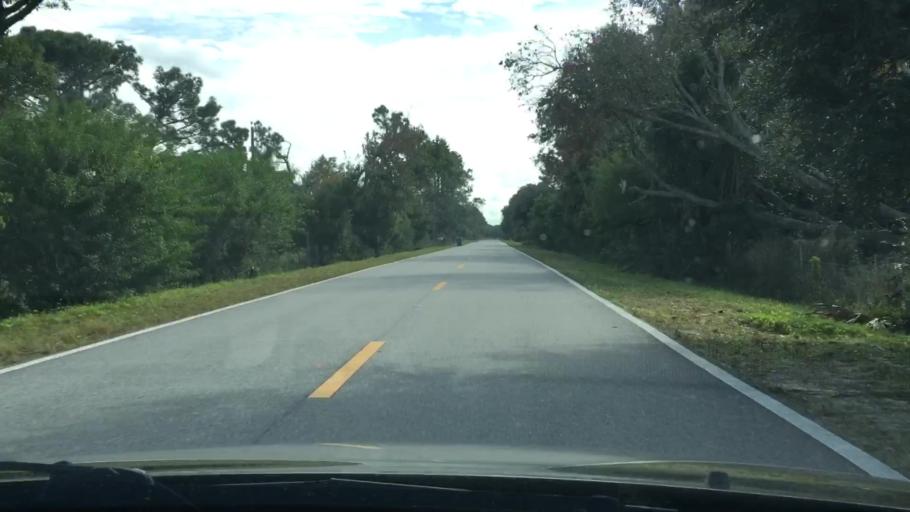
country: US
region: Florida
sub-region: Volusia County
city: Ormond Beach
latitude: 29.2978
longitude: -81.1296
